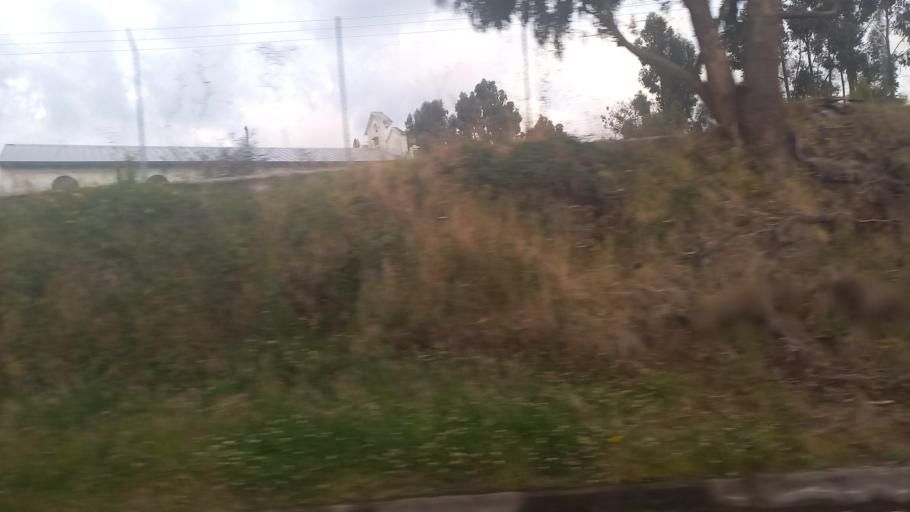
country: EC
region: Pichincha
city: Cayambe
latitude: 0.0905
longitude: -78.1005
